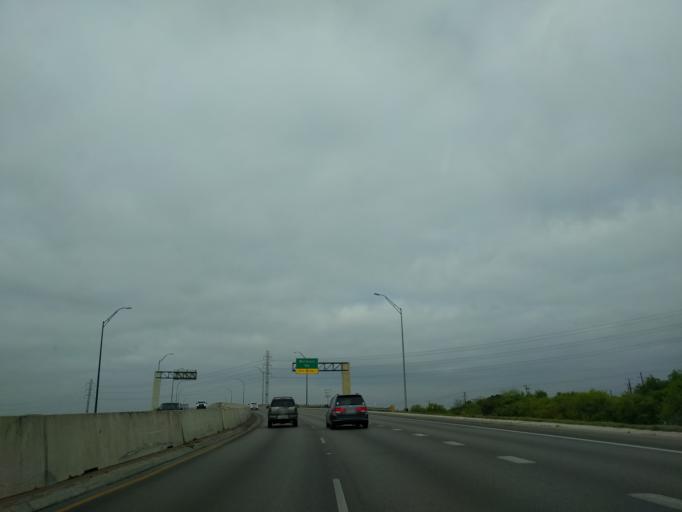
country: US
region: Texas
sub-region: Bexar County
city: Windcrest
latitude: 29.5462
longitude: -98.4326
